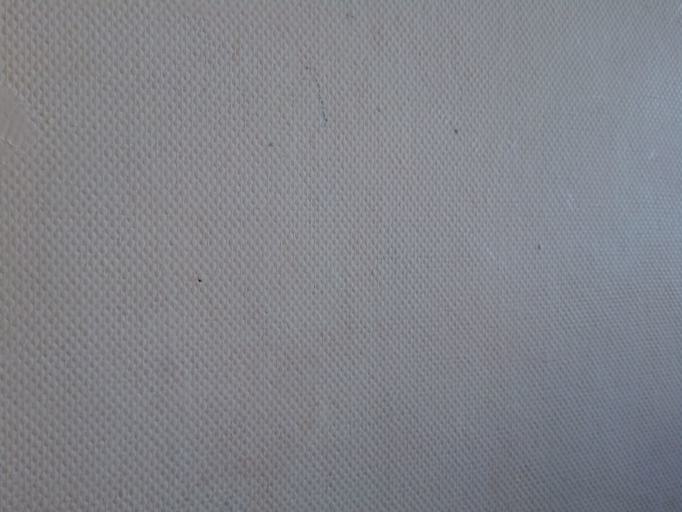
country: RU
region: Moscow
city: Vatutino
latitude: 55.8544
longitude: 37.6998
